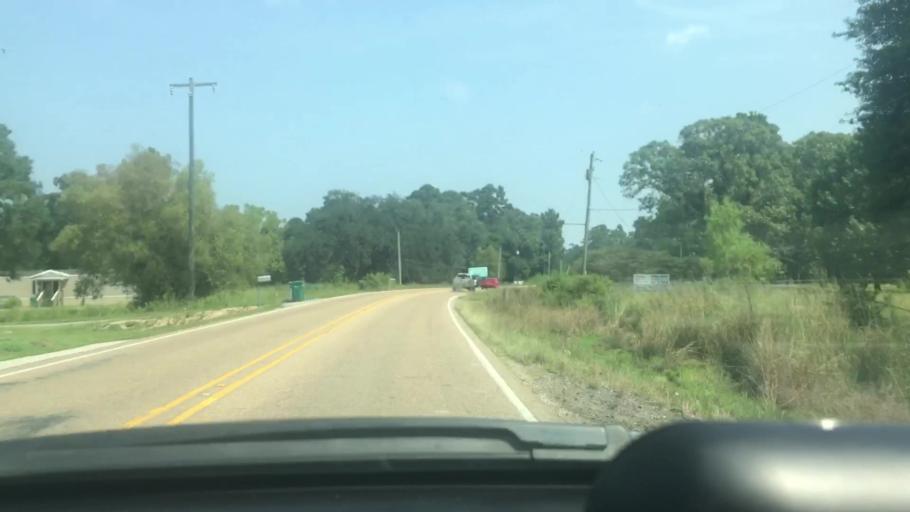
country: US
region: Louisiana
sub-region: Livingston Parish
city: Denham Springs
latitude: 30.4741
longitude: -90.9190
